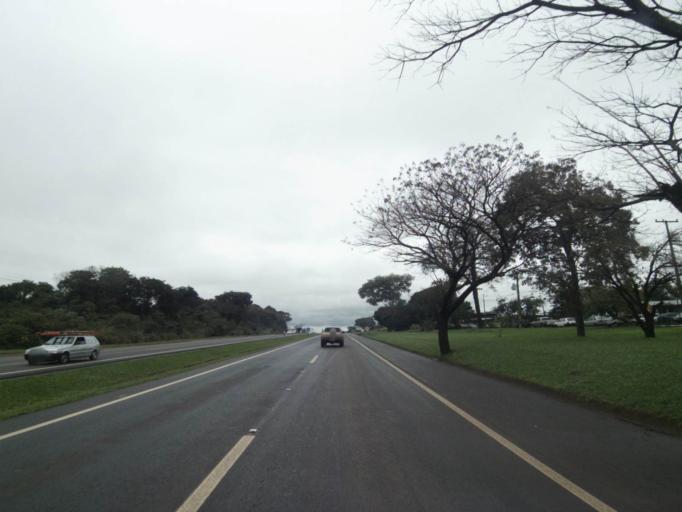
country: BR
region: Parana
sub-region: Foz Do Iguacu
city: Foz do Iguacu
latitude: -25.5102
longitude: -54.5657
